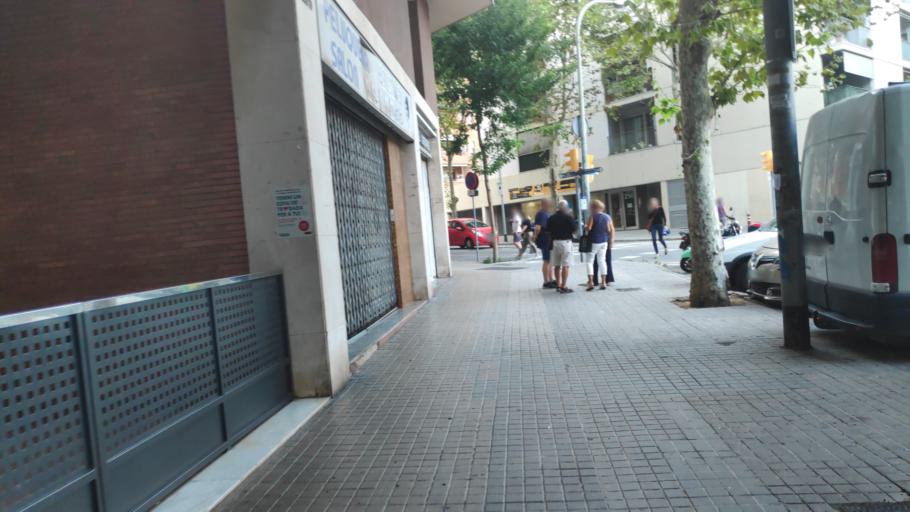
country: ES
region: Catalonia
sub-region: Provincia de Barcelona
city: Sant Marti
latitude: 41.4111
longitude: 2.1923
